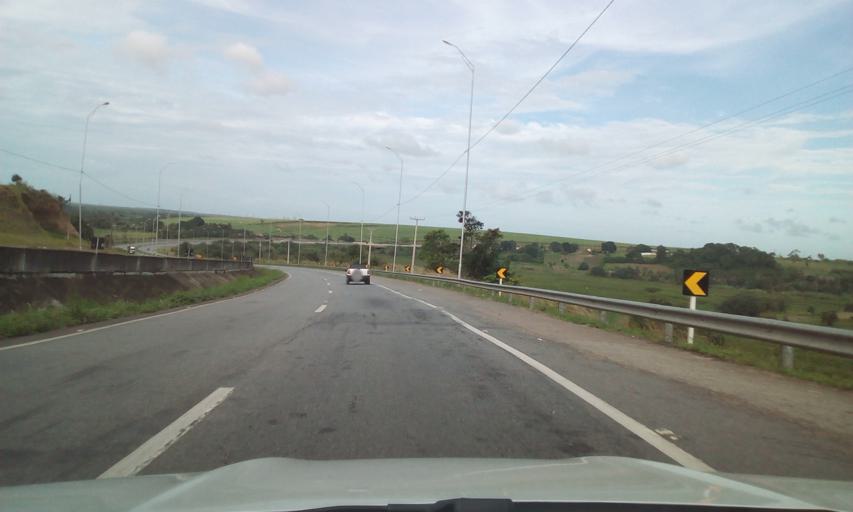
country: BR
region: Paraiba
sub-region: Santa Rita
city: Santa Rita
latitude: -7.0846
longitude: -34.9781
